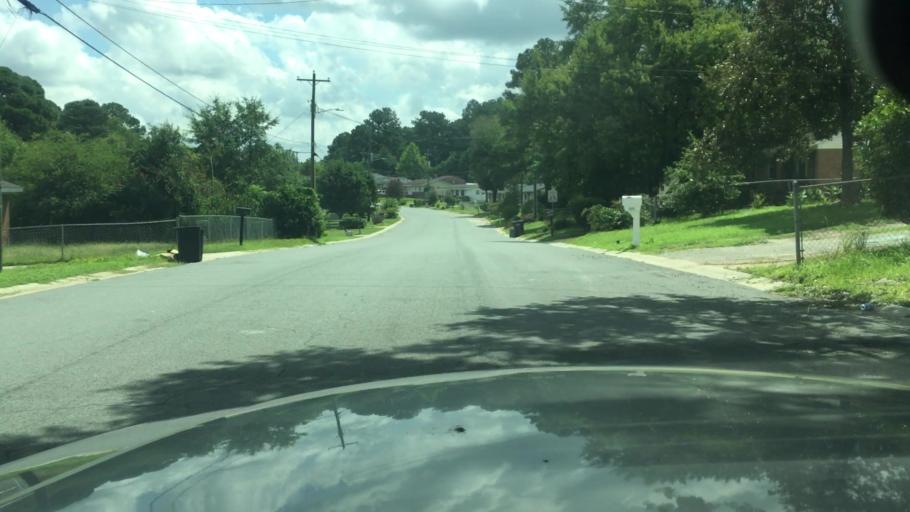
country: US
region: North Carolina
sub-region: Cumberland County
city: Fayetteville
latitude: 35.0257
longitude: -78.9207
